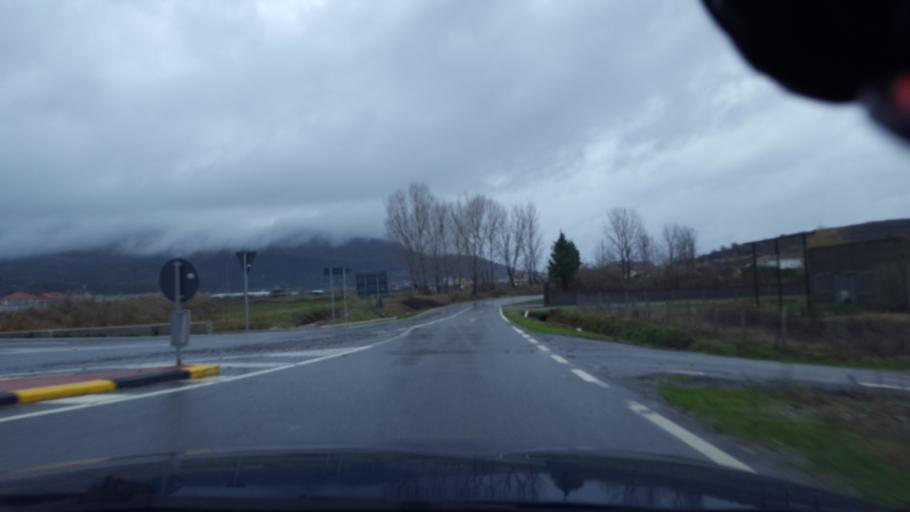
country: AL
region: Shkoder
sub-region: Rrethi i Shkodres
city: Berdica e Madhe
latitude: 42.0058
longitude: 19.4796
